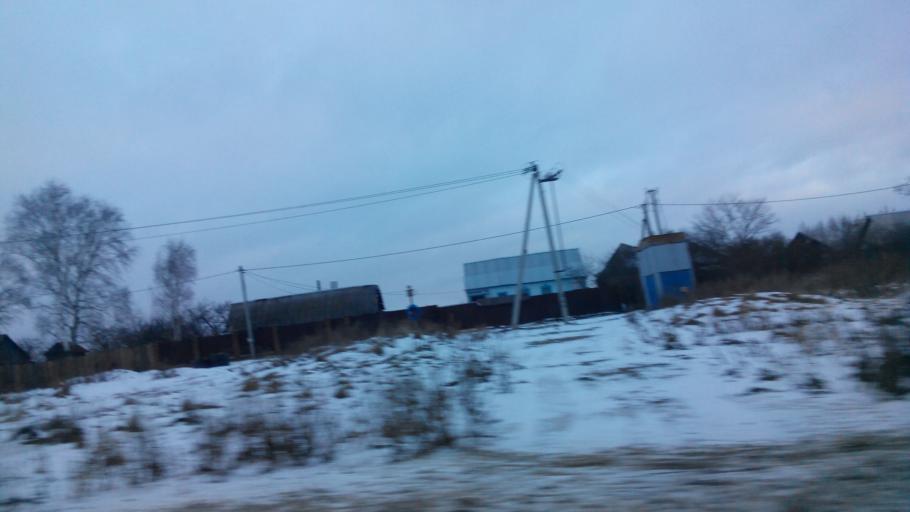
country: RU
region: Tula
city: Mayskiy
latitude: 53.9739
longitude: 38.2445
